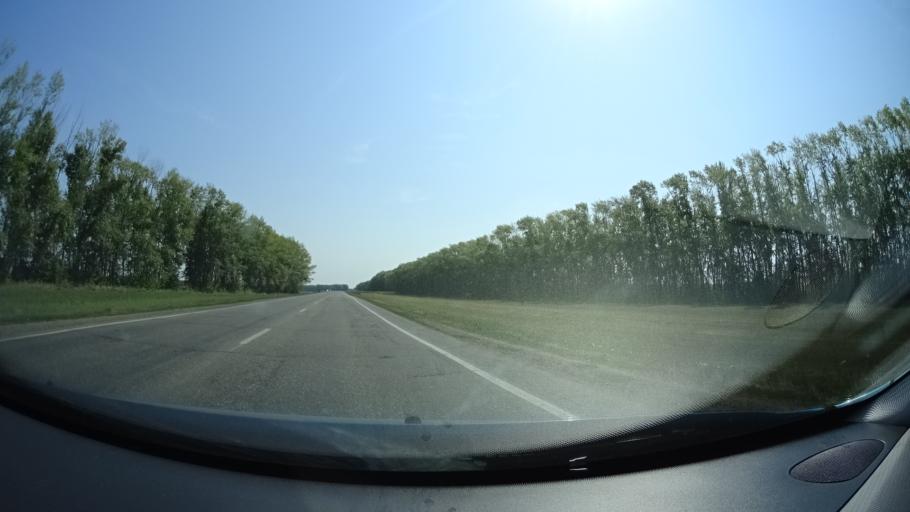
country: RU
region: Bashkortostan
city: Karmaskaly
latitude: 54.3909
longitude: 56.1224
